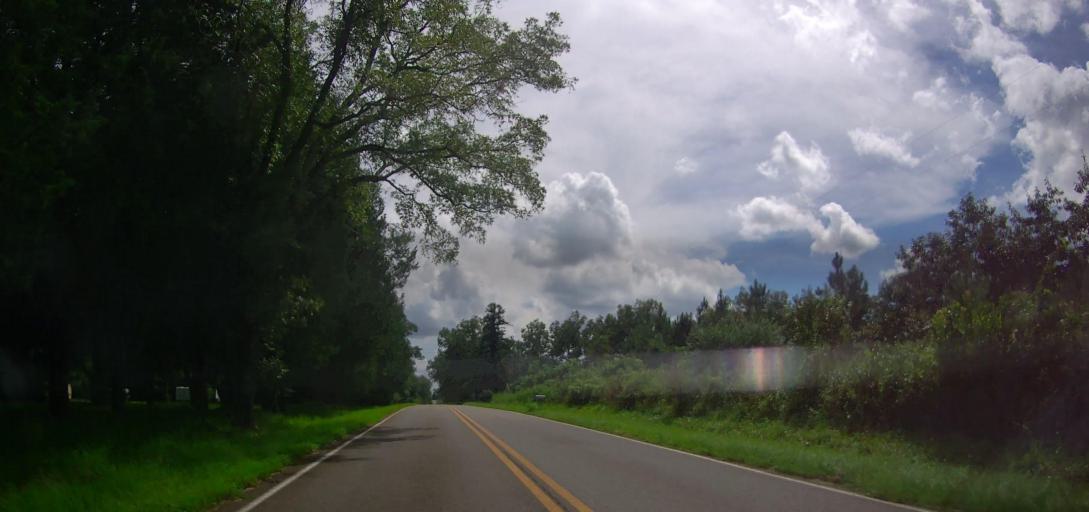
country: US
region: Georgia
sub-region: Taylor County
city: Butler
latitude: 32.4913
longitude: -84.2056
